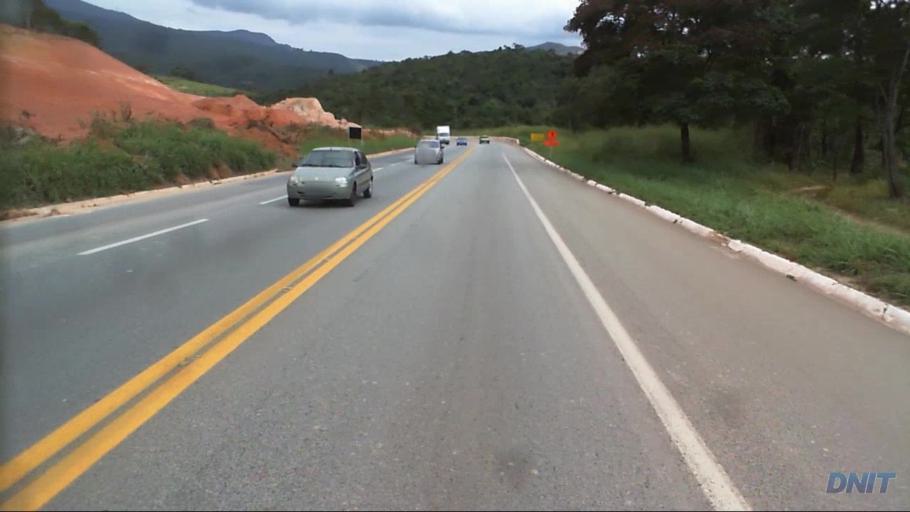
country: BR
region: Minas Gerais
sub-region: Caete
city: Caete
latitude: -19.7770
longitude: -43.6549
